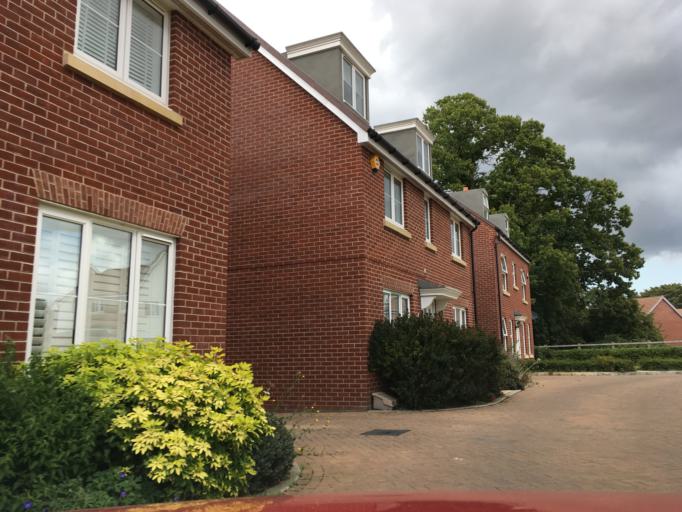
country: GB
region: England
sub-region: Kent
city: Maidstone
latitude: 51.2576
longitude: 0.5200
